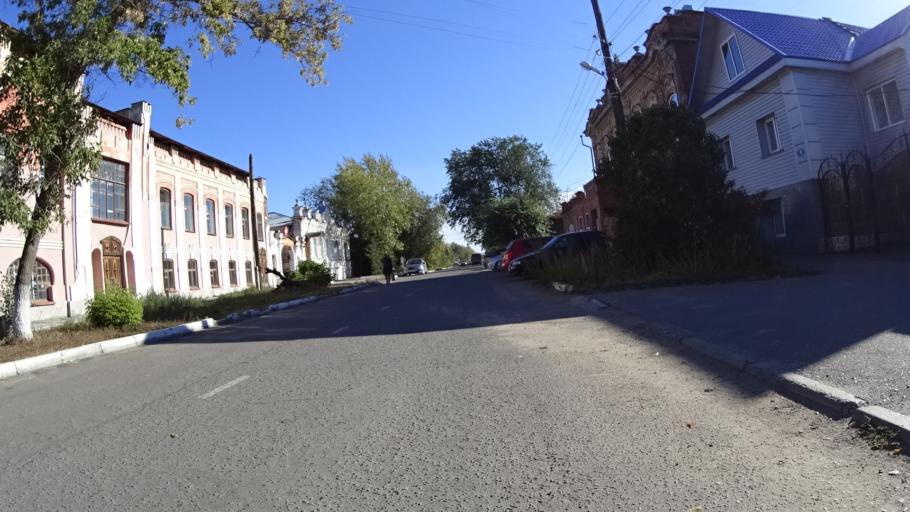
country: RU
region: Chelyabinsk
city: Troitsk
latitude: 54.0832
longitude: 61.5552
